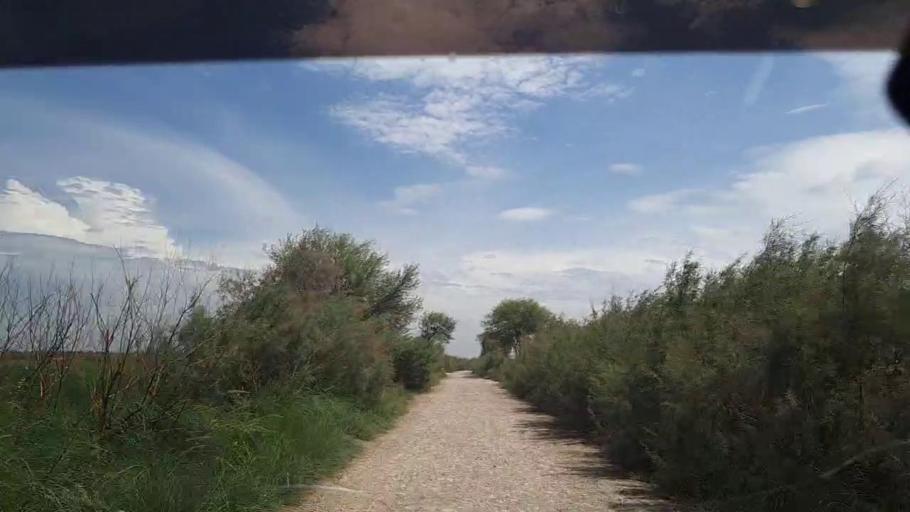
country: PK
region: Sindh
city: Ghauspur
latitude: 28.1455
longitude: 68.9776
